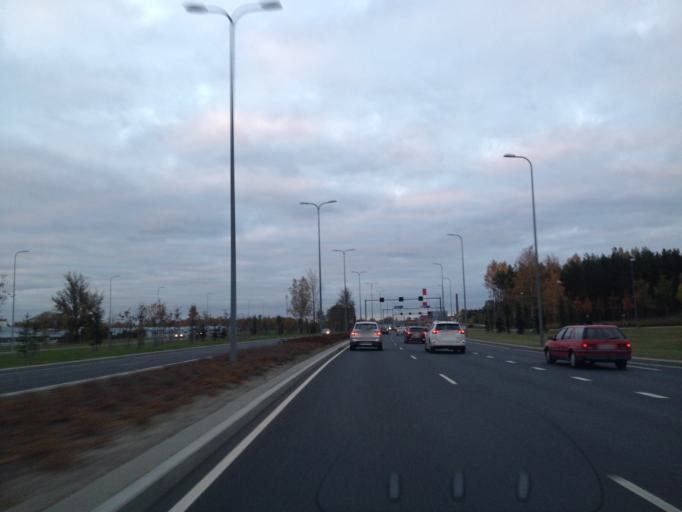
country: EE
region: Harju
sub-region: Tallinna linn
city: Tallinn
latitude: 59.4149
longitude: 24.7609
